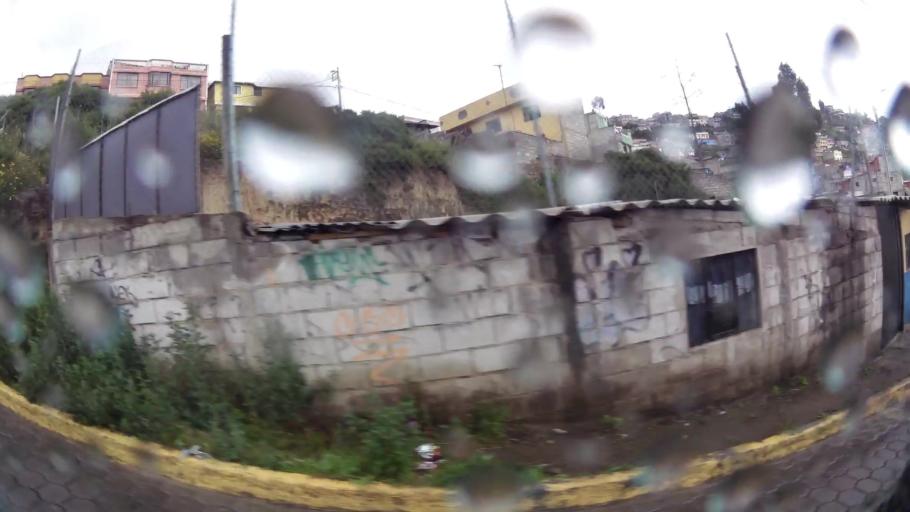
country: EC
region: Pichincha
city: Quito
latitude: -0.0964
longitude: -78.5082
